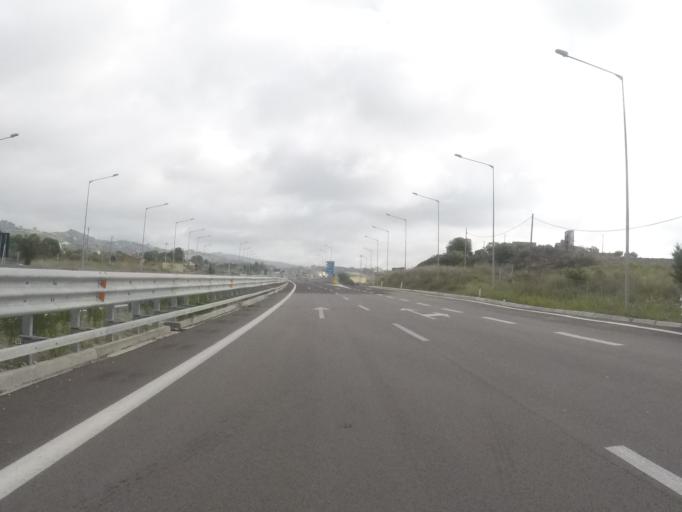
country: IT
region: Sicily
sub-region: Agrigento
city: Grotte
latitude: 37.3728
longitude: 13.7149
